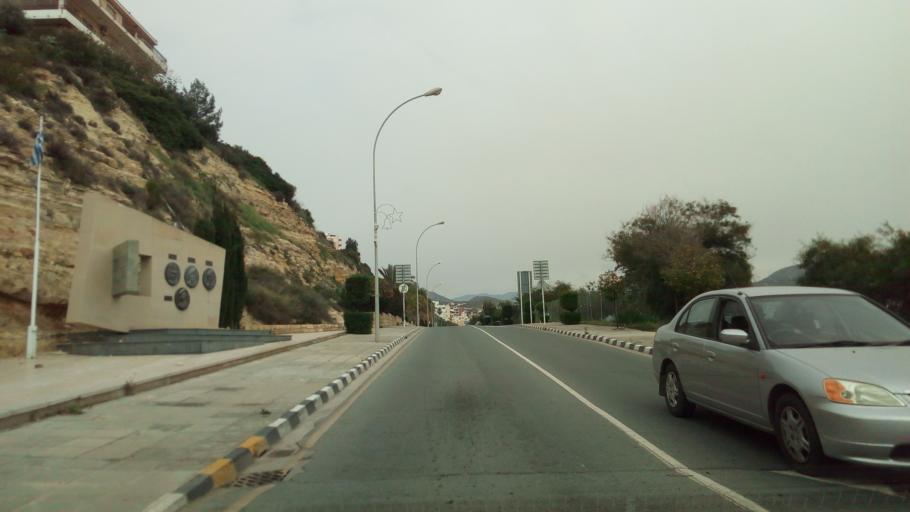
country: CY
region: Limassol
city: Mouttagiaka
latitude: 34.7111
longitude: 33.0874
